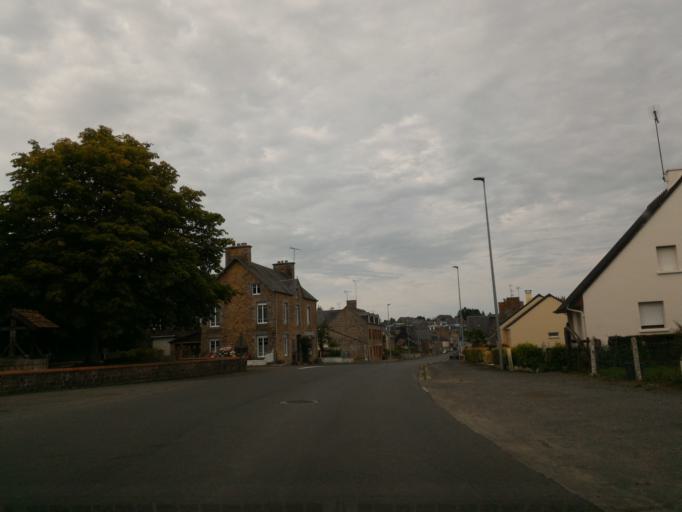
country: FR
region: Lower Normandy
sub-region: Departement de la Manche
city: La Haye-Pesnel
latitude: 48.7918
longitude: -1.4018
